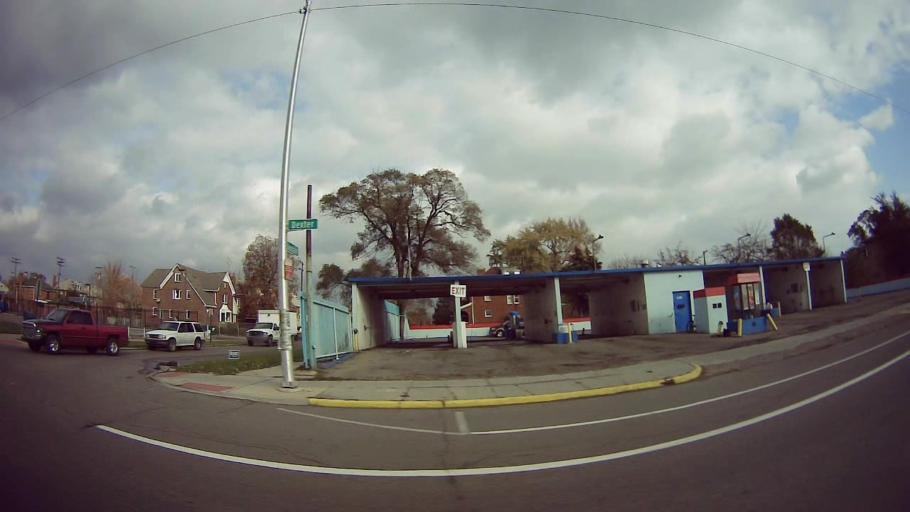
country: US
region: Michigan
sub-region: Wayne County
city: Highland Park
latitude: 42.3868
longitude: -83.1288
